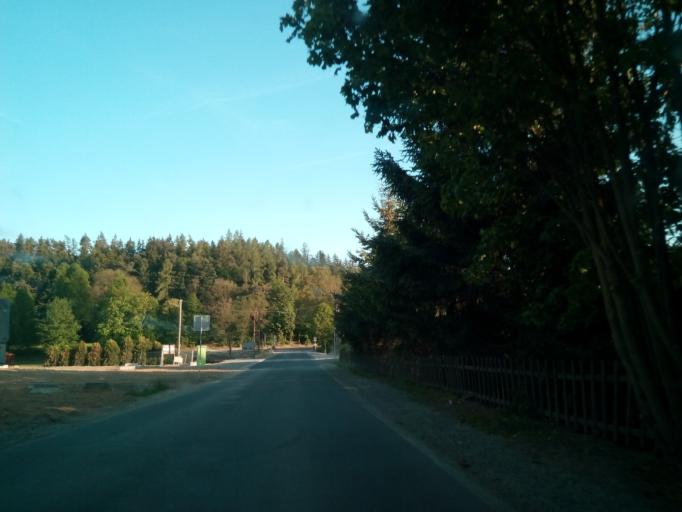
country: CZ
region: South Moravian
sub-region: Okres Blansko
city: Jedovnice
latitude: 49.3393
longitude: 16.7486
